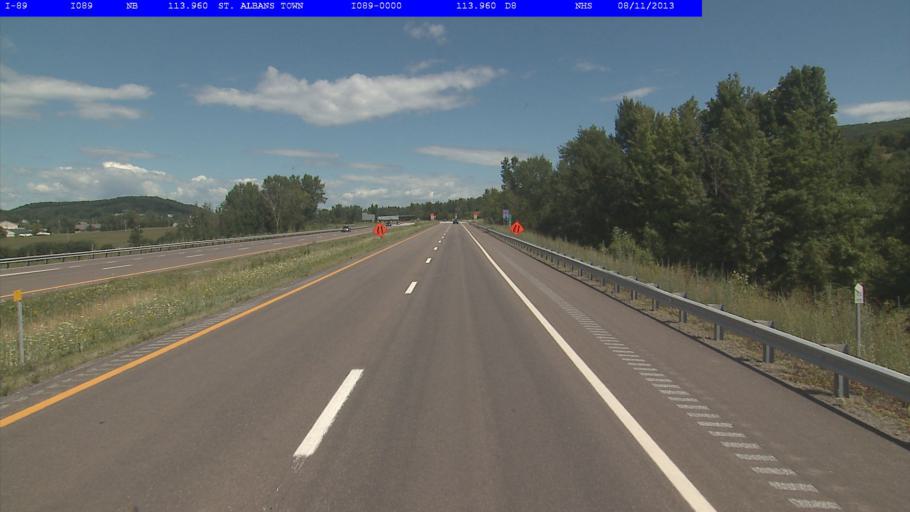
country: US
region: Vermont
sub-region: Franklin County
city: Saint Albans
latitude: 44.7976
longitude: -73.0677
